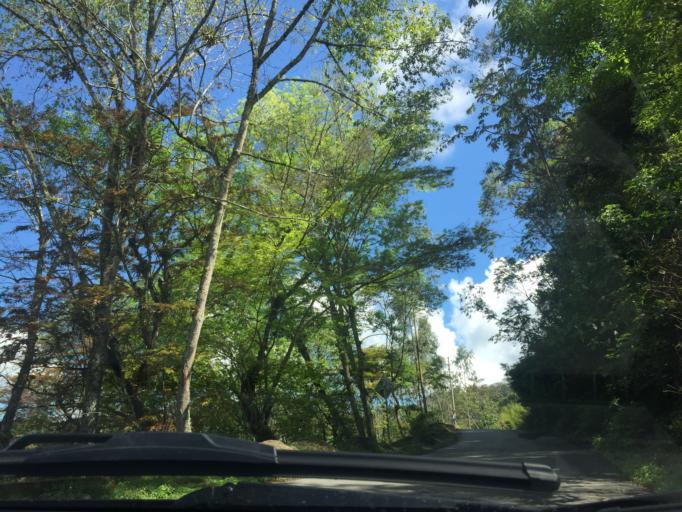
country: CO
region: Cundinamarca
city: San Francisco
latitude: 4.9995
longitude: -74.2826
